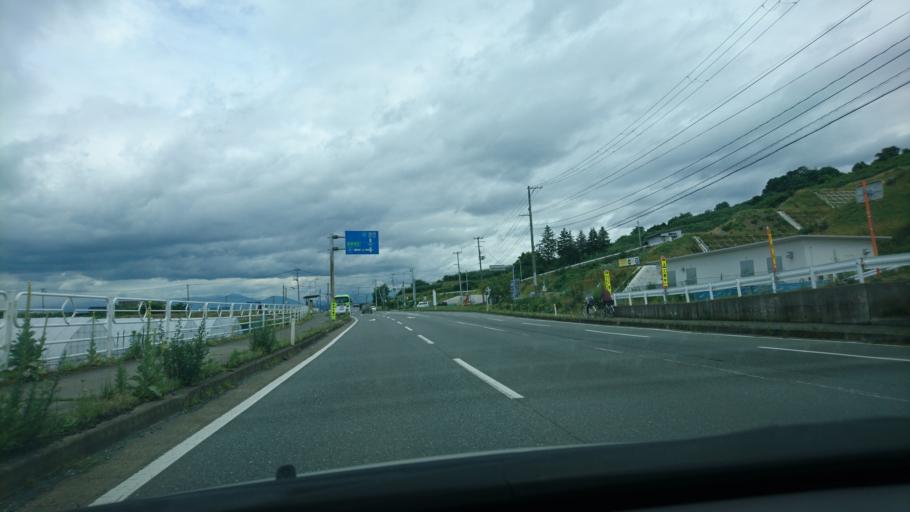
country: JP
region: Iwate
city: Morioka-shi
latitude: 39.6601
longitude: 141.1785
